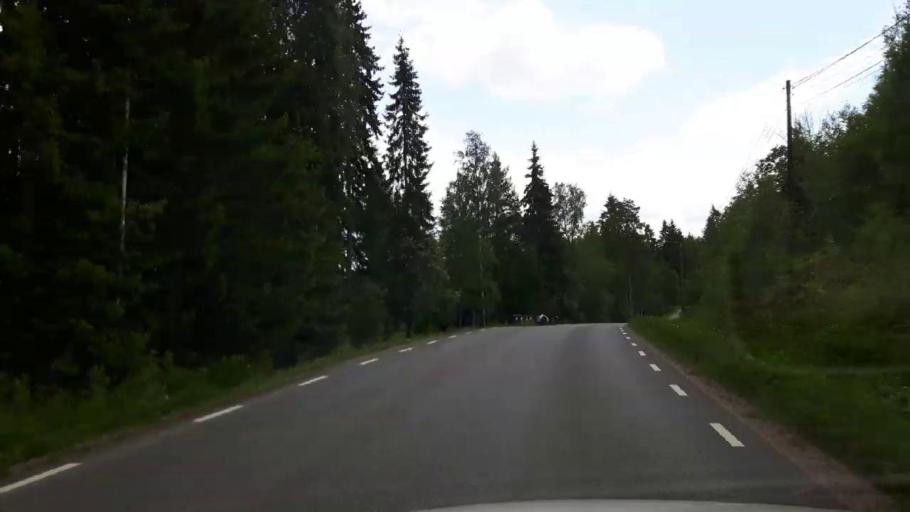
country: SE
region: Dalarna
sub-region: Faluns Kommun
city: Falun
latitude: 60.6634
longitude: 15.7602
